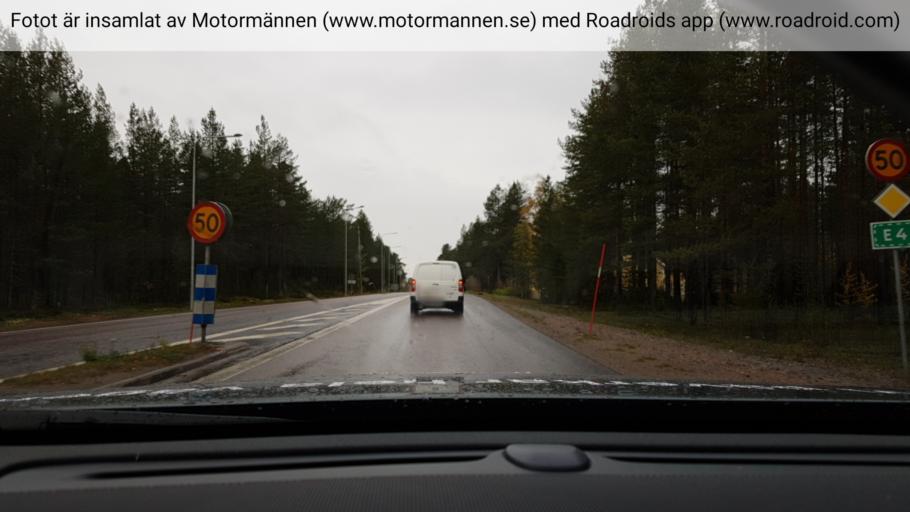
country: SE
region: Norrbotten
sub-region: Lulea Kommun
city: Bergnaset
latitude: 65.5807
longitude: 22.0734
